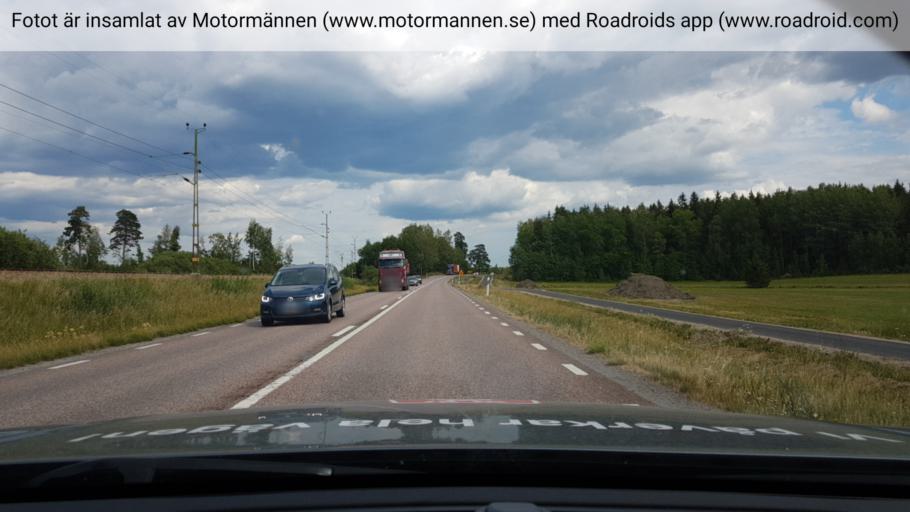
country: SE
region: Uppsala
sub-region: Heby Kommun
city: Heby
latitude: 59.9368
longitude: 16.9007
